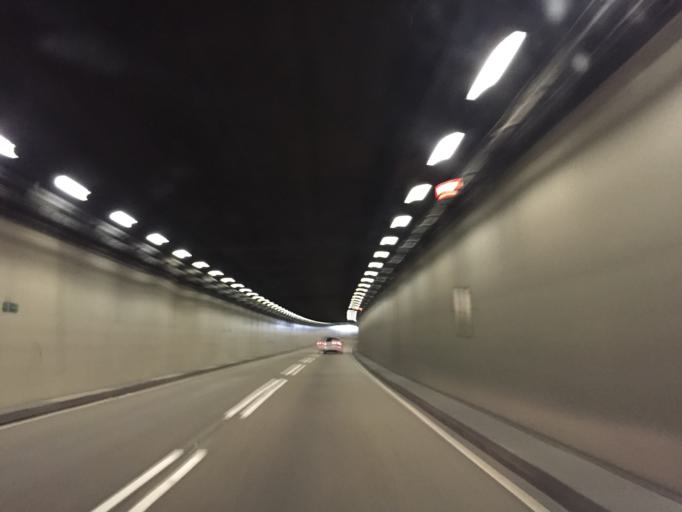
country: NL
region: North Holland
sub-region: Gemeente Aalsmeer
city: Aalsmeer
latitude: 52.3163
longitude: 4.7535
